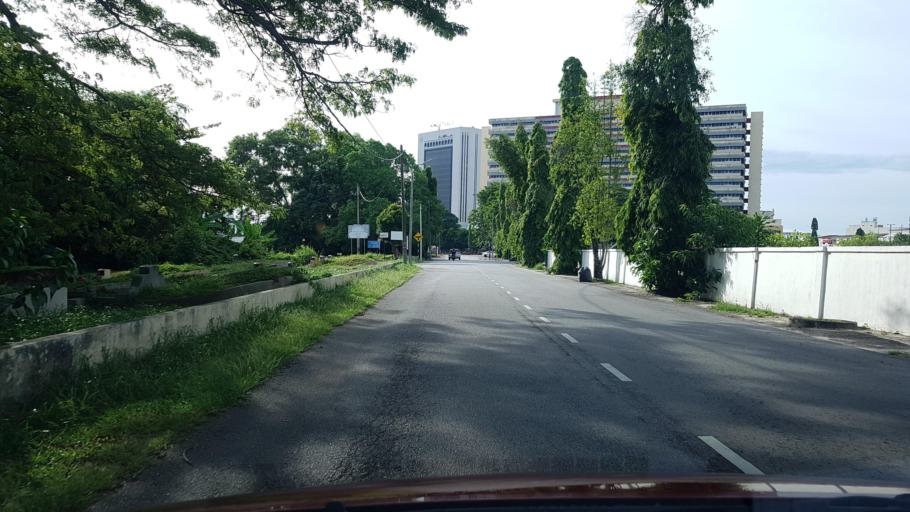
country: MY
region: Terengganu
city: Kuala Terengganu
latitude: 5.3263
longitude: 103.1433
